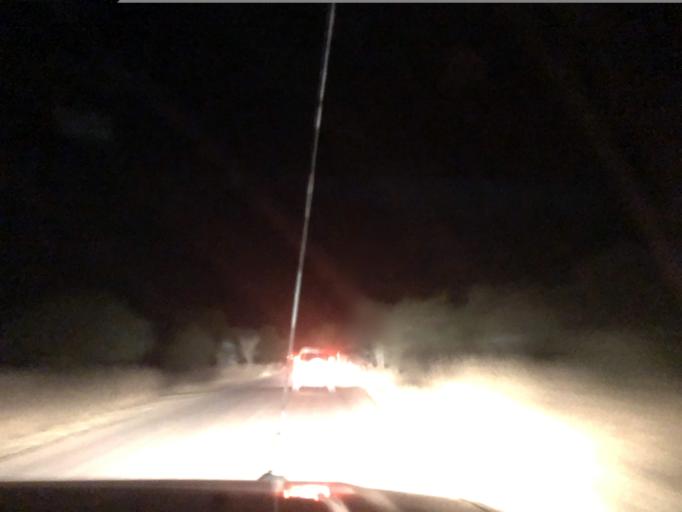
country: CM
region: Far North
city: Kousseri
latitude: 11.5282
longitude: 15.2914
